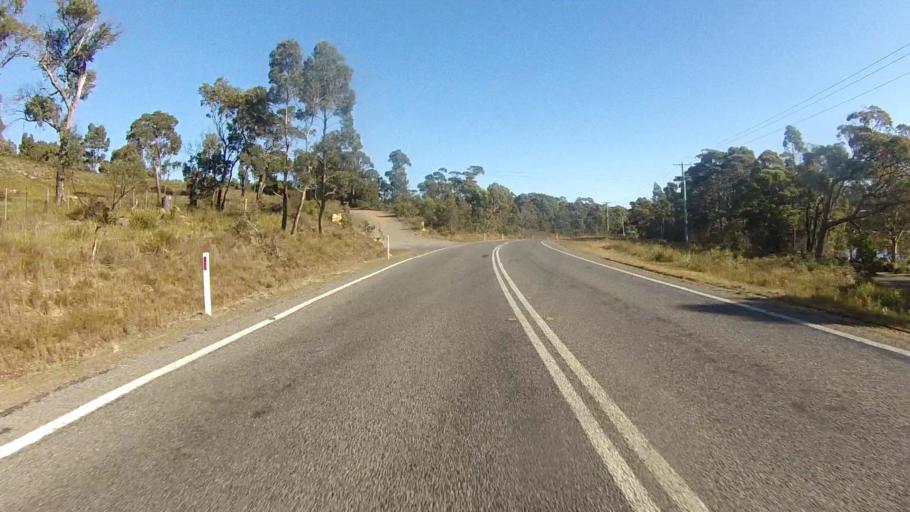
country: AU
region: Tasmania
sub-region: Clarence
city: Sandford
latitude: -43.0207
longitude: 147.9067
